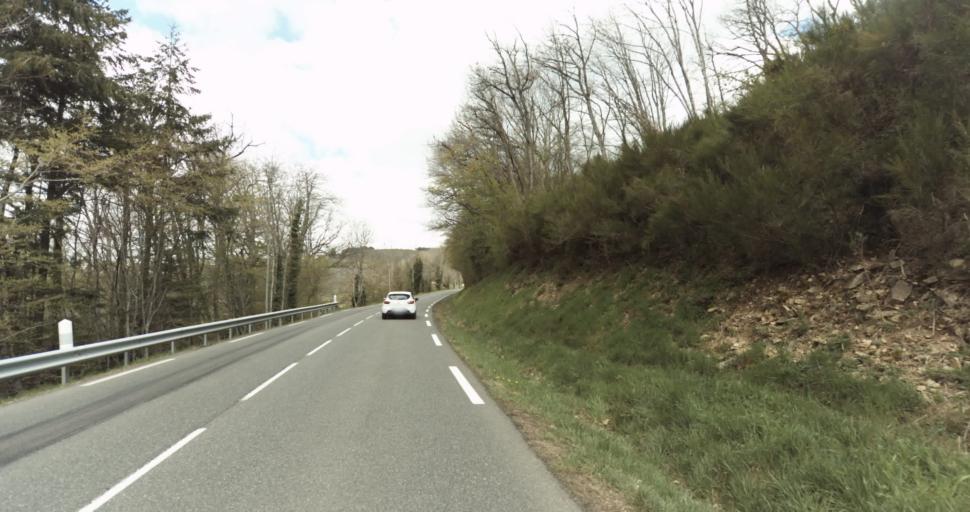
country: FR
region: Rhone-Alpes
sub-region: Departement du Rhone
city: Tarare
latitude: 45.9263
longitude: 4.4006
